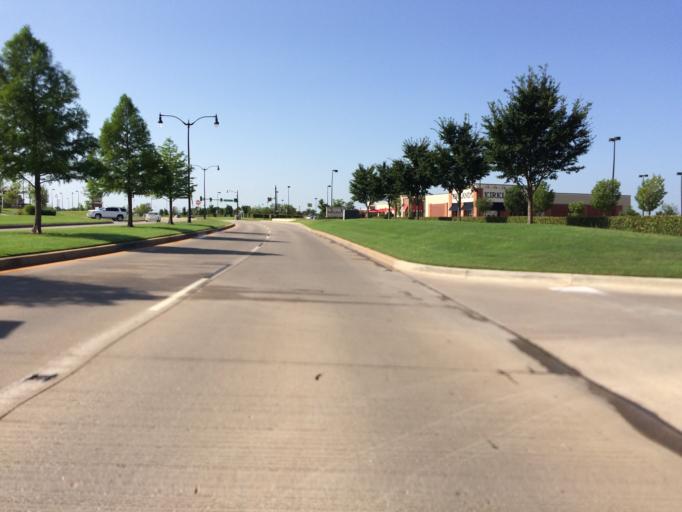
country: US
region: Oklahoma
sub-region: Cleveland County
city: Norman
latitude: 35.2389
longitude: -97.4825
